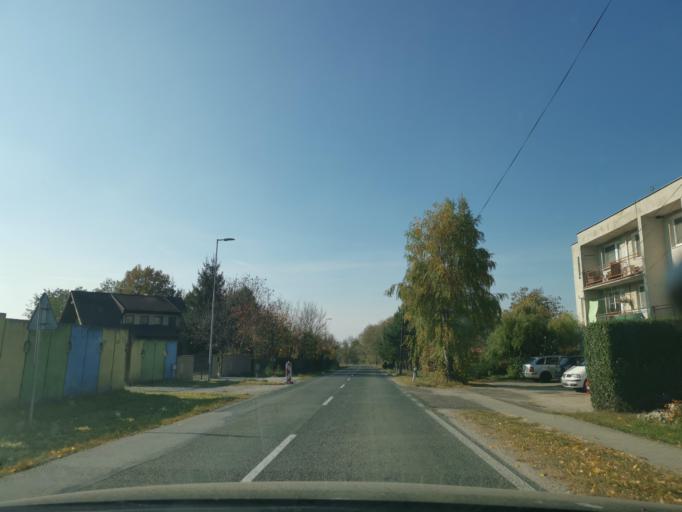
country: SK
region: Trnavsky
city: Gbely
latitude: 48.5773
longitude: 17.1813
